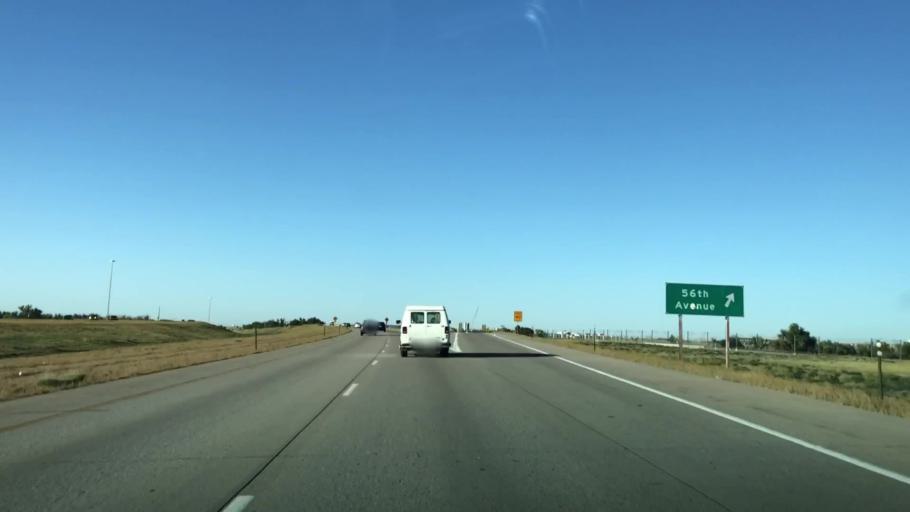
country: US
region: Colorado
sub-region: Adams County
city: Aurora
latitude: 39.7937
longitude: -104.7874
